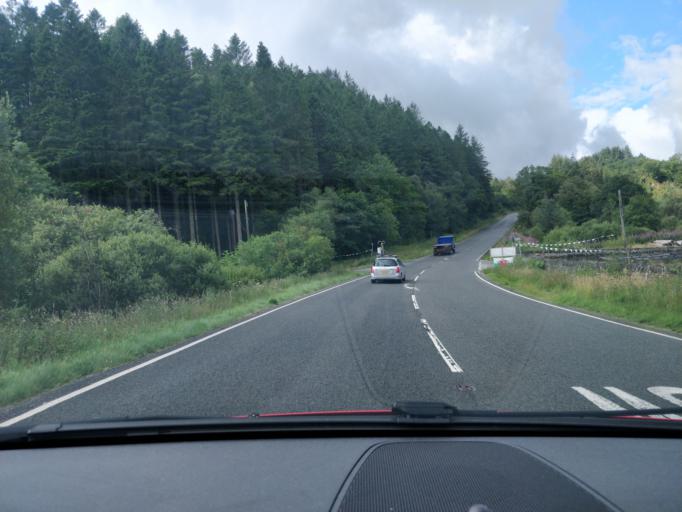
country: GB
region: Wales
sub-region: Gwynedd
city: Blaenau-Ffestiniog
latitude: 53.0436
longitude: -3.9160
